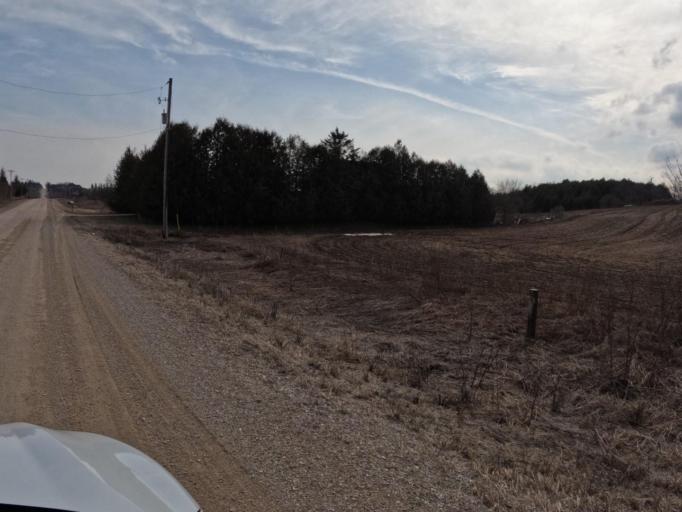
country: CA
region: Ontario
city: Orangeville
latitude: 43.8974
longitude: -80.3007
